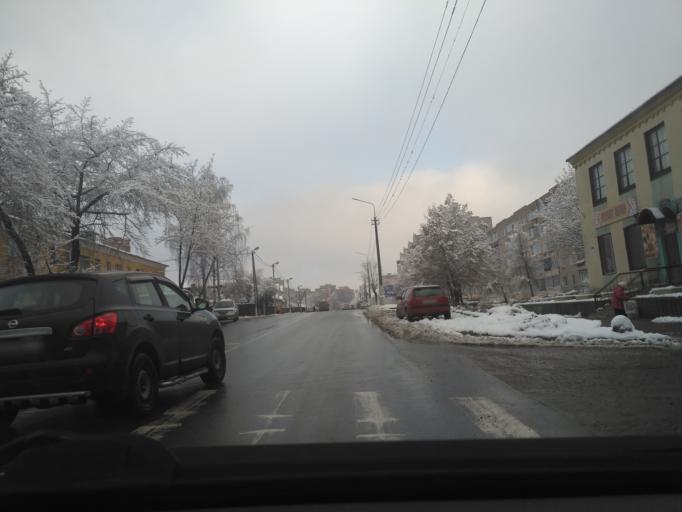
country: BY
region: Minsk
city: Horad Barysaw
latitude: 54.2173
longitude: 28.5009
